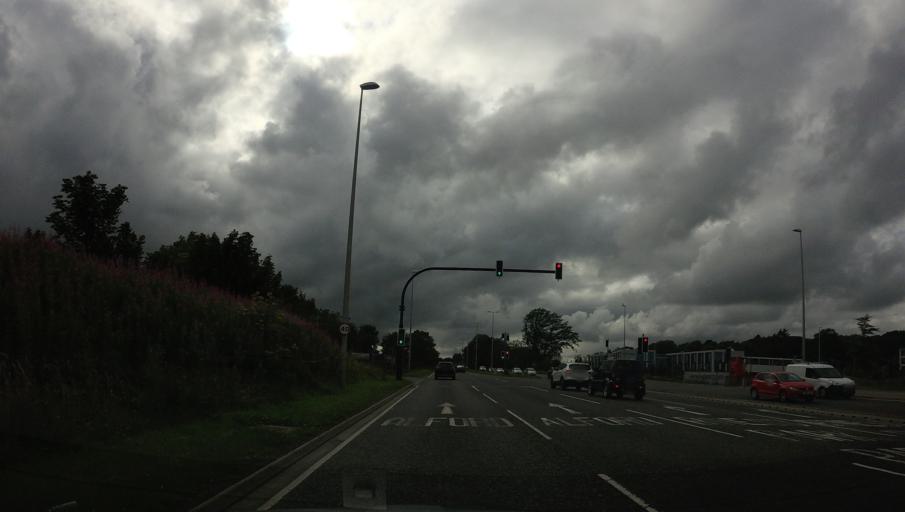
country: GB
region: Scotland
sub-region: Aberdeenshire
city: Westhill
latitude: 57.1466
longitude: -2.2239
